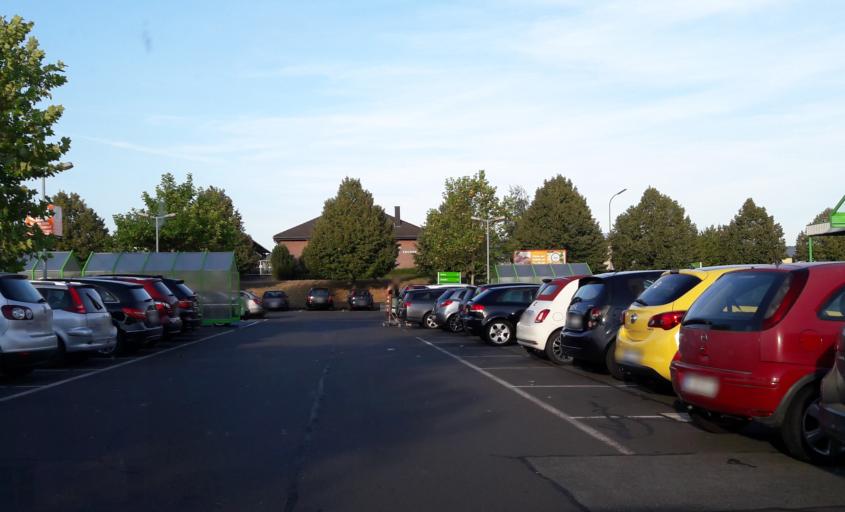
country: DE
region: Rheinland-Pfalz
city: Briedel
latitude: 50.0263
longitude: 7.1576
